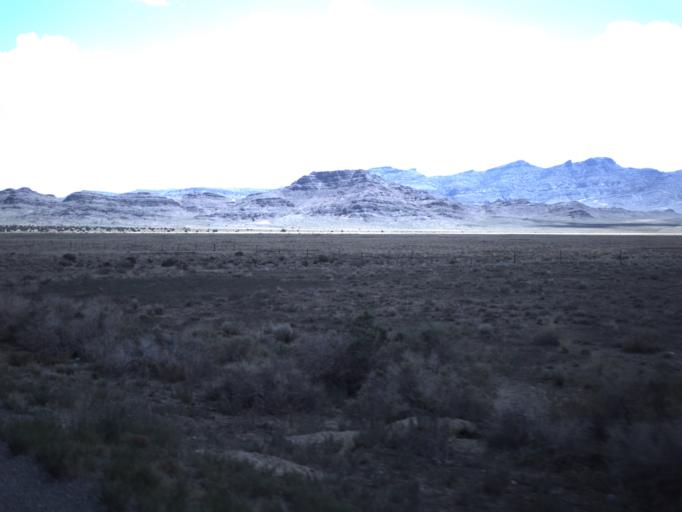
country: US
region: Utah
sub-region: Beaver County
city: Milford
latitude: 39.0620
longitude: -113.7516
